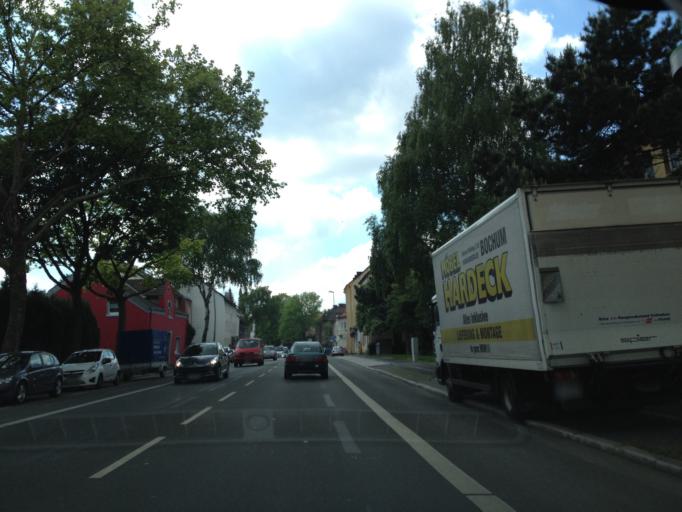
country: DE
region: North Rhine-Westphalia
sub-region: Regierungsbezirk Arnsberg
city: Bochum
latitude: 51.4440
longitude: 7.2200
